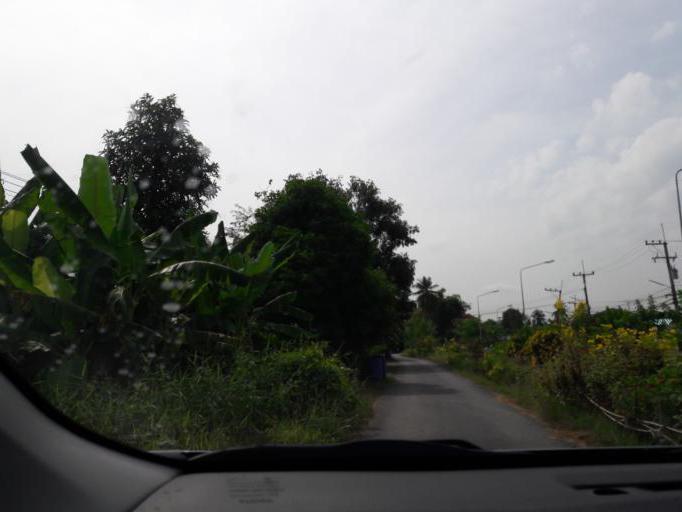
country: TH
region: Ang Thong
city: Ang Thong
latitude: 14.5775
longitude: 100.4751
